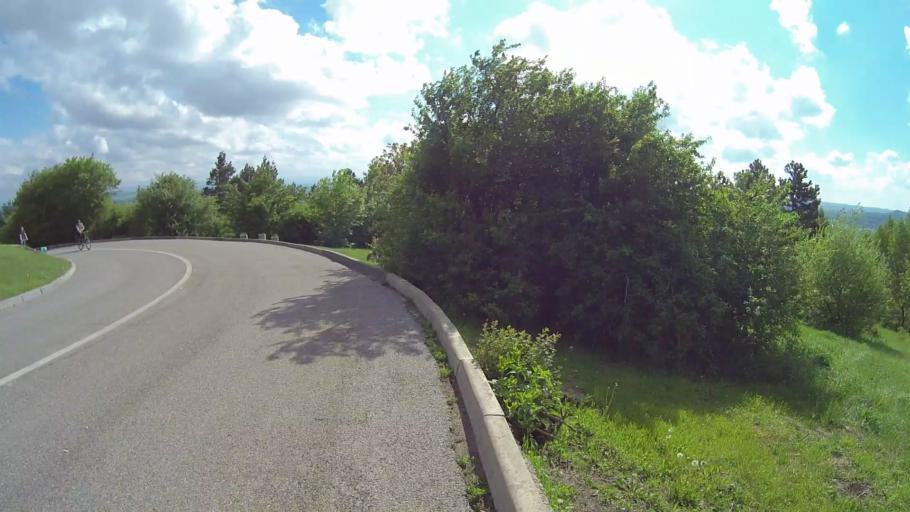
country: RU
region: Stavropol'skiy
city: Pyatigorsk
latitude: 44.0502
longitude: 43.0772
